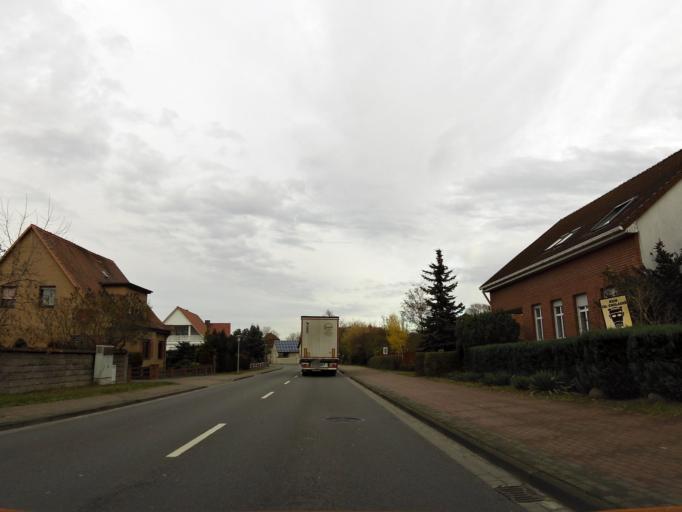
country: DE
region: Saxony-Anhalt
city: Pretzier
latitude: 52.7913
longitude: 11.2327
